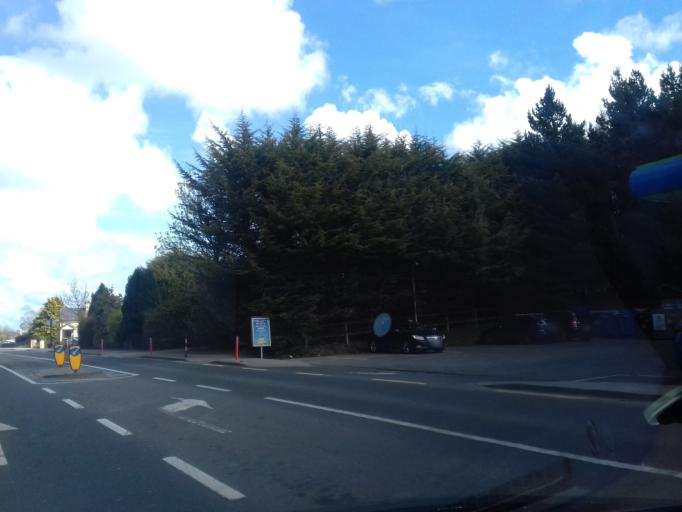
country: IE
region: Ulster
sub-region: An Cabhan
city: Ballyjamesduff
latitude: 53.9648
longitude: -7.2298
